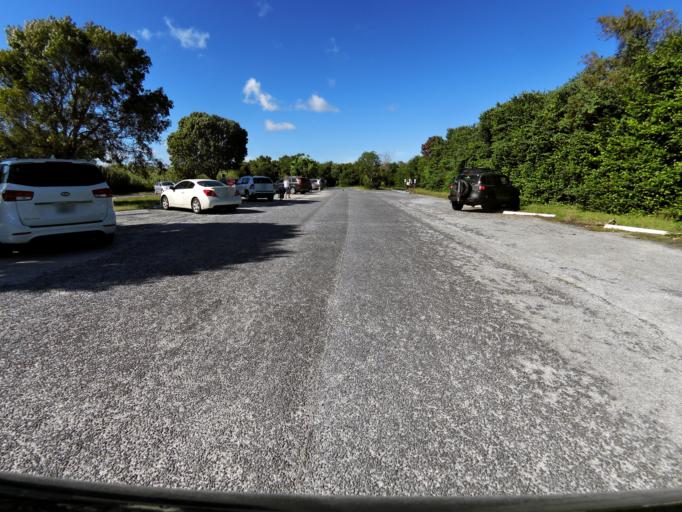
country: US
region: Florida
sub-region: Miami-Dade County
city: Florida City
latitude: 25.4404
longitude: -80.7830
